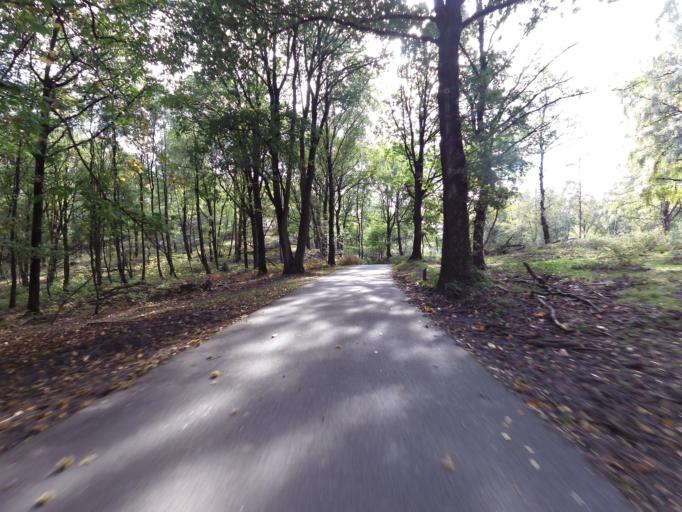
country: NL
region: Gelderland
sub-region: Gemeente Rheden
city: Rheden
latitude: 52.0165
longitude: 6.0132
